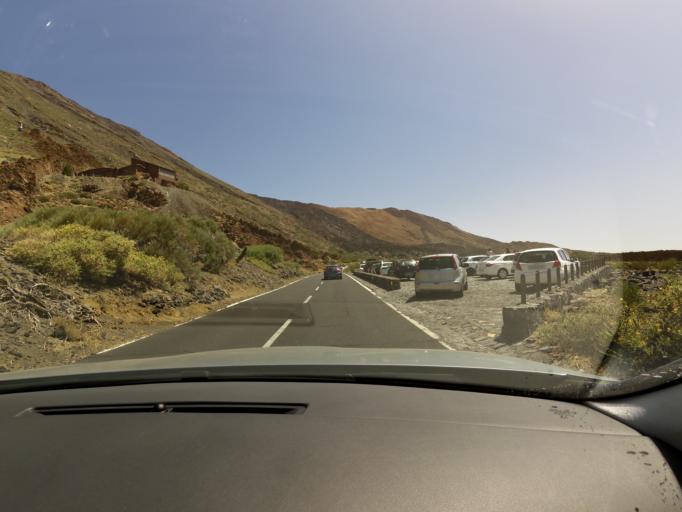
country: ES
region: Canary Islands
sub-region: Provincia de Santa Cruz de Tenerife
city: Vilaflor
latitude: 28.2524
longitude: -16.6258
